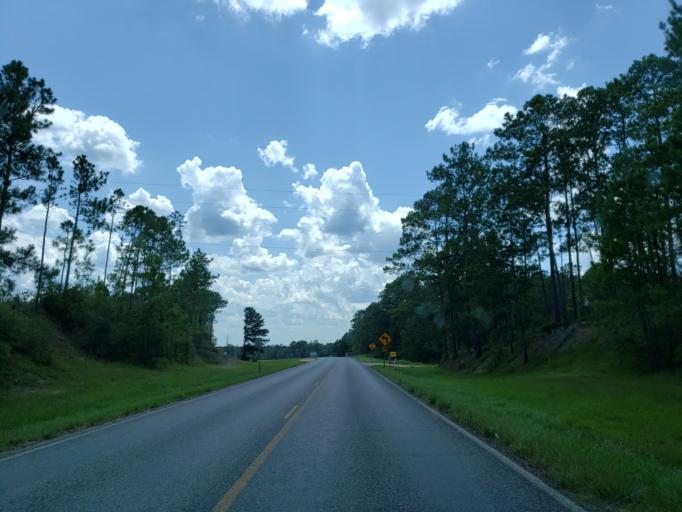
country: US
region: Mississippi
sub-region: Greene County
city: Leakesville
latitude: 31.1083
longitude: -88.7796
